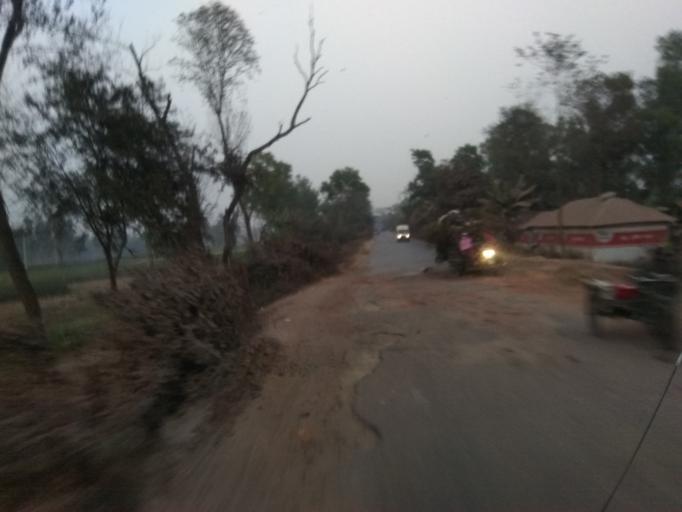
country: BD
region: Rajshahi
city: Bogra
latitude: 24.7473
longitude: 89.3396
